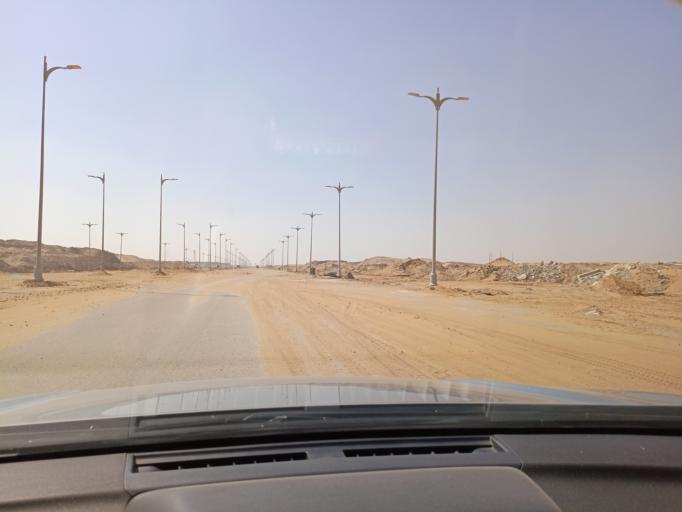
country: EG
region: Muhafazat al Qalyubiyah
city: Al Khankah
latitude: 30.0085
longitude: 31.6221
